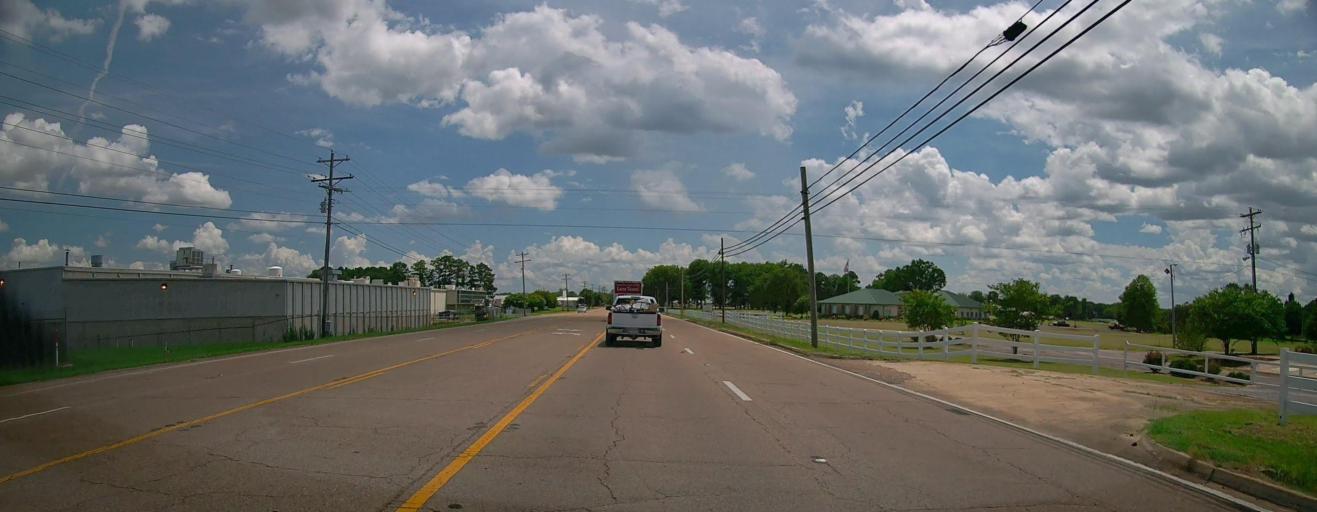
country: US
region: Mississippi
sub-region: Lee County
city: Verona
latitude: 34.1674
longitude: -88.7196
